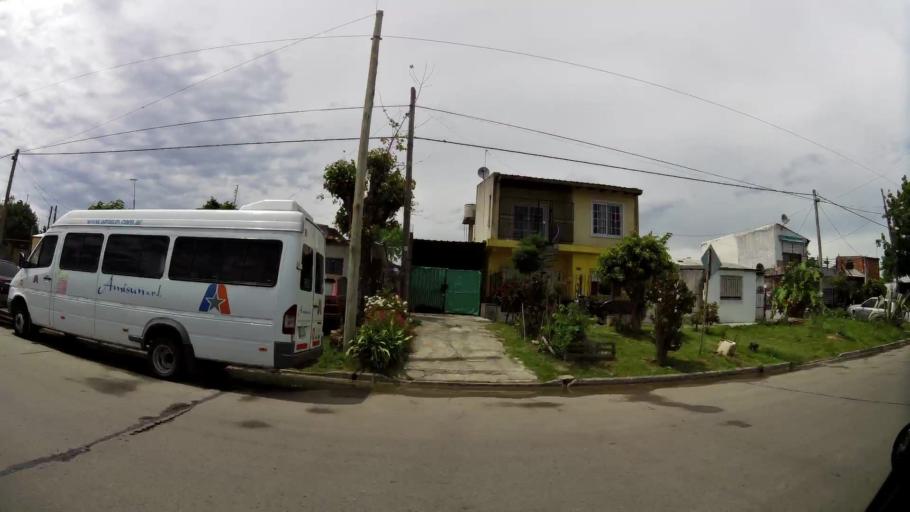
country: AR
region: Buenos Aires
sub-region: Partido de Quilmes
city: Quilmes
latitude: -34.7705
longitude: -58.2353
